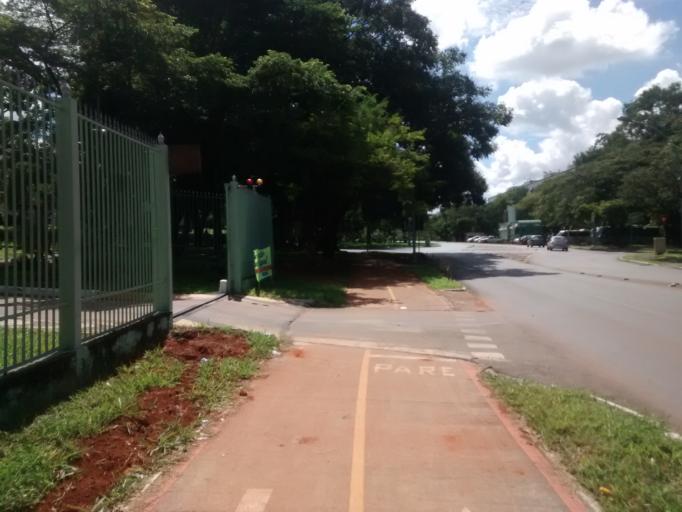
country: BR
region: Federal District
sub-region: Brasilia
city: Brasilia
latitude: -15.7773
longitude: -47.8846
